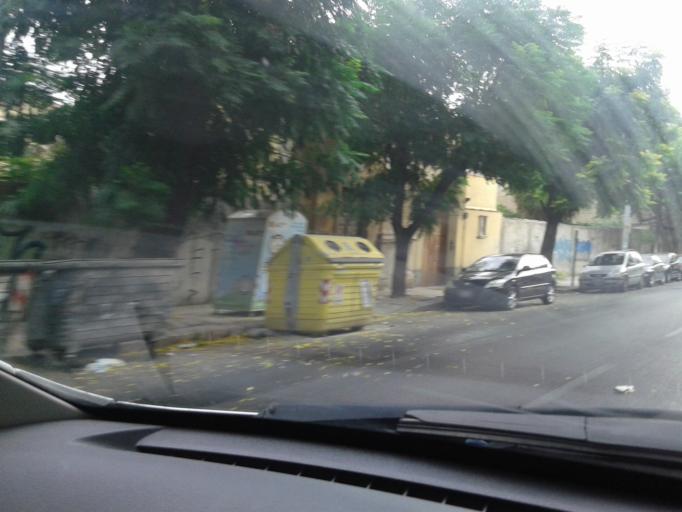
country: IT
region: Sicily
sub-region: Palermo
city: Palermo
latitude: 38.1012
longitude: 13.3256
